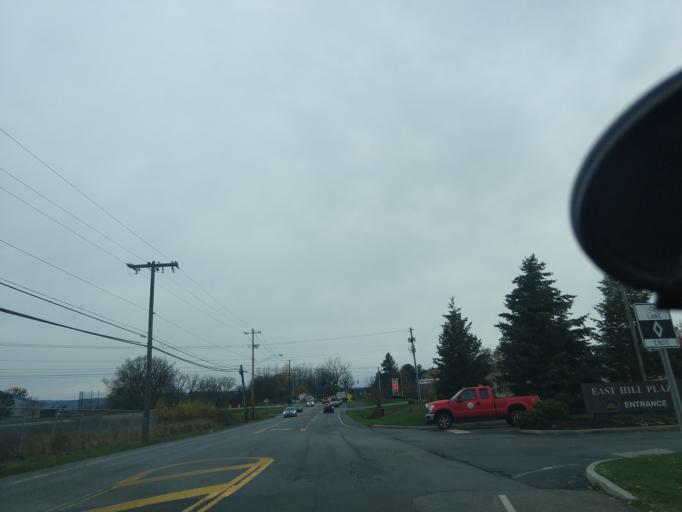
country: US
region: New York
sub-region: Tompkins County
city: East Ithaca
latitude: 42.4359
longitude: -76.4626
